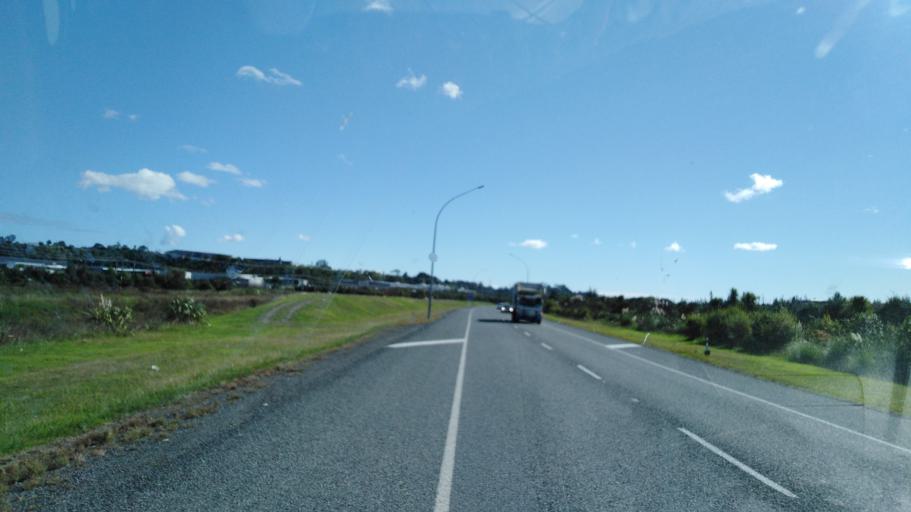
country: NZ
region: Bay of Plenty
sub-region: Tauranga City
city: Tauranga
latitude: -37.7490
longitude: 176.1034
